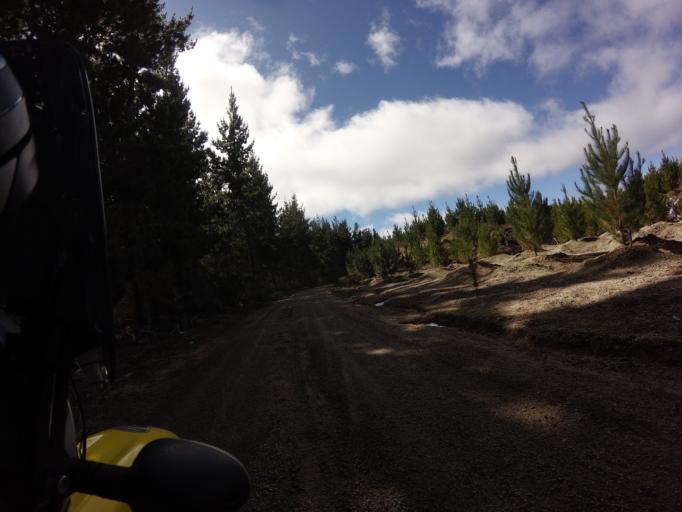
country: NZ
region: Bay of Plenty
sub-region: Whakatane District
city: Murupara
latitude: -38.8194
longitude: 176.5538
